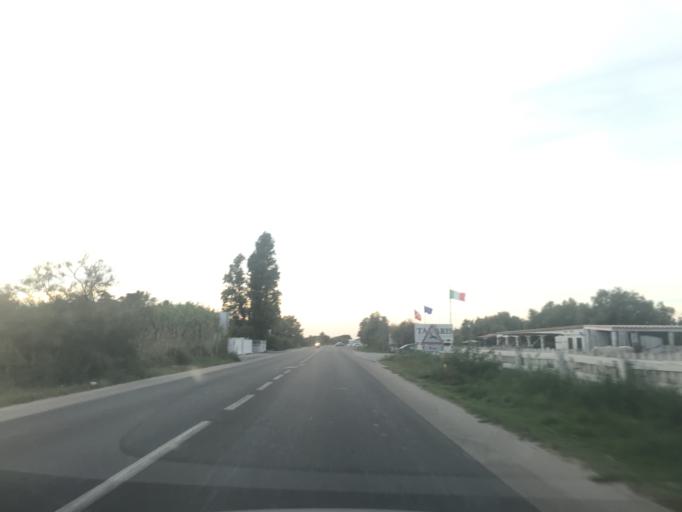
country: FR
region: Provence-Alpes-Cote d'Azur
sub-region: Departement des Bouches-du-Rhone
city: Saintes-Maries-de-la-Mer
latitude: 43.4593
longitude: 4.4246
